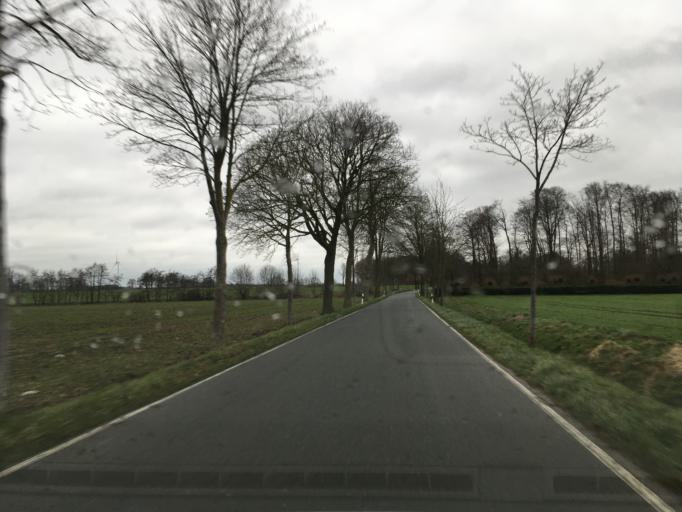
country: DE
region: North Rhine-Westphalia
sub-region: Regierungsbezirk Munster
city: Schoppingen
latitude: 52.0837
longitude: 7.1694
